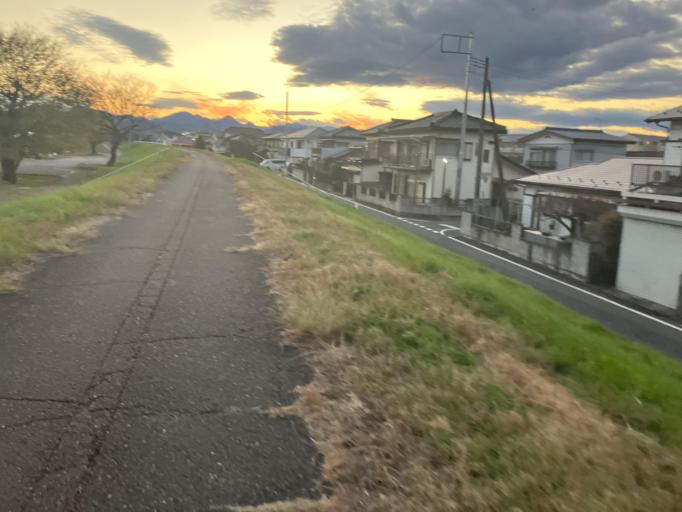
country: JP
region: Gunma
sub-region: Sawa-gun
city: Tamamura
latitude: 36.2680
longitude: 139.1143
